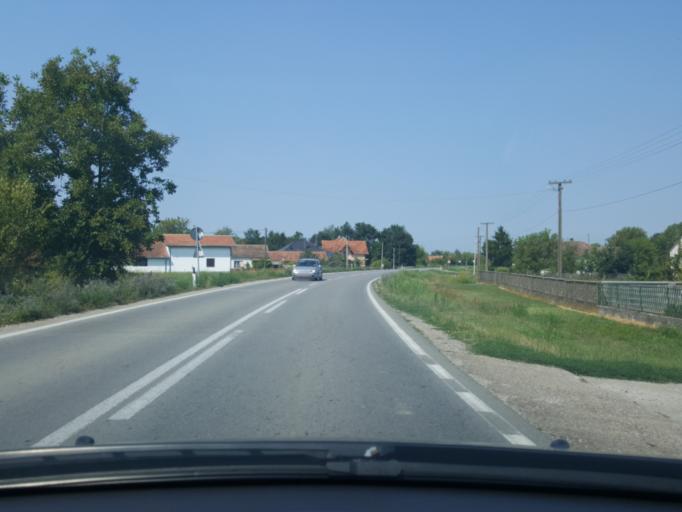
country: RS
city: Bogosavac
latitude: 44.7542
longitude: 19.5696
